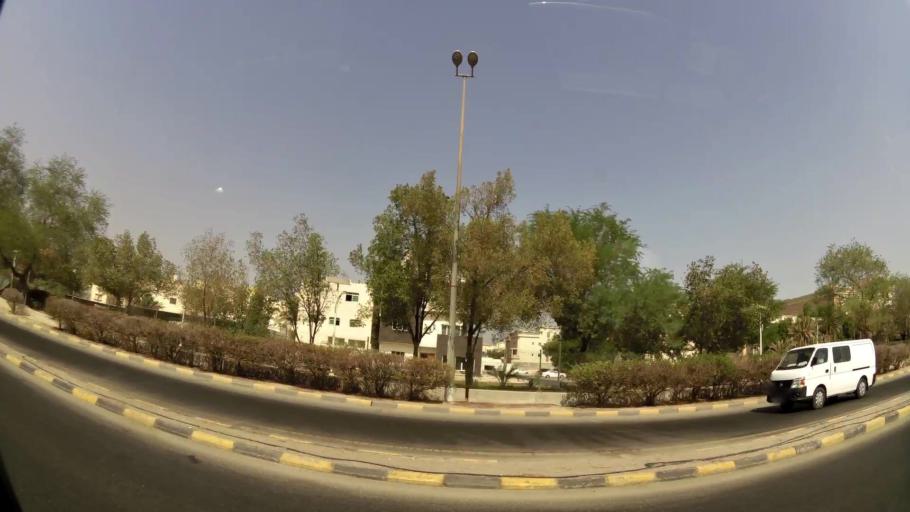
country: KW
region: Al Asimah
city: Ash Shamiyah
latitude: 29.3321
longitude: 47.9687
